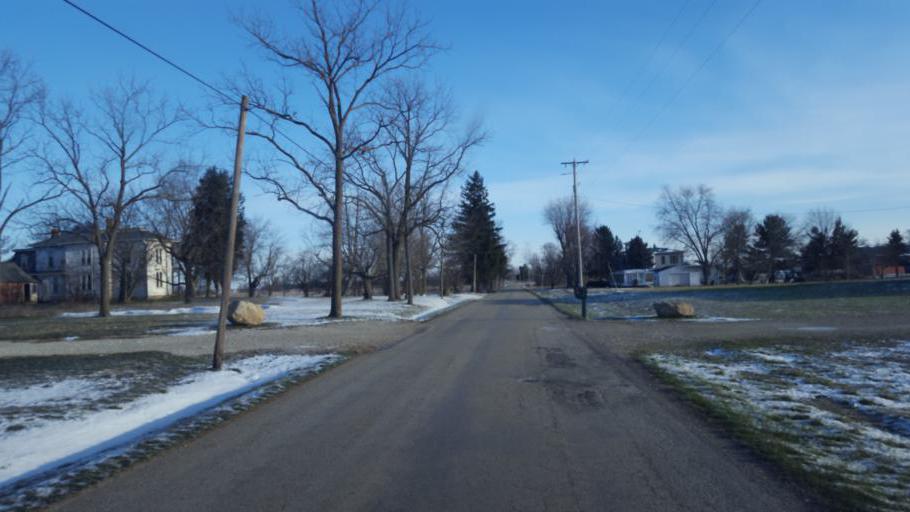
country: US
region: Ohio
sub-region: Morrow County
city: Cardington
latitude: 40.5761
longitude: -82.9190
